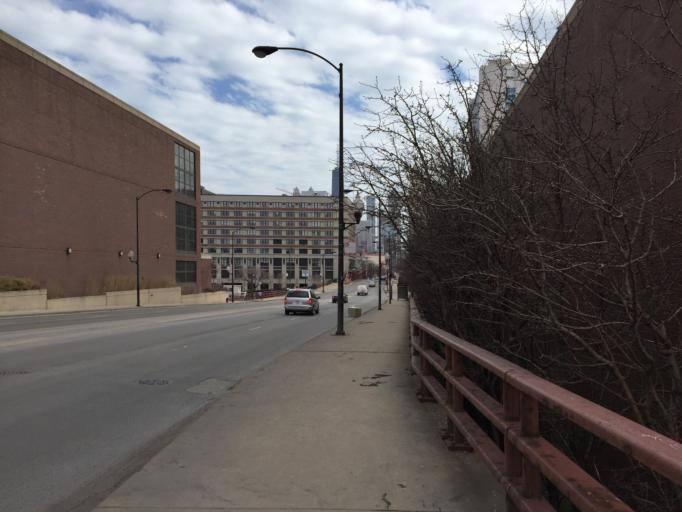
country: US
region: Illinois
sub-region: Cook County
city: Chicago
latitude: 41.8964
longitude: -87.6467
